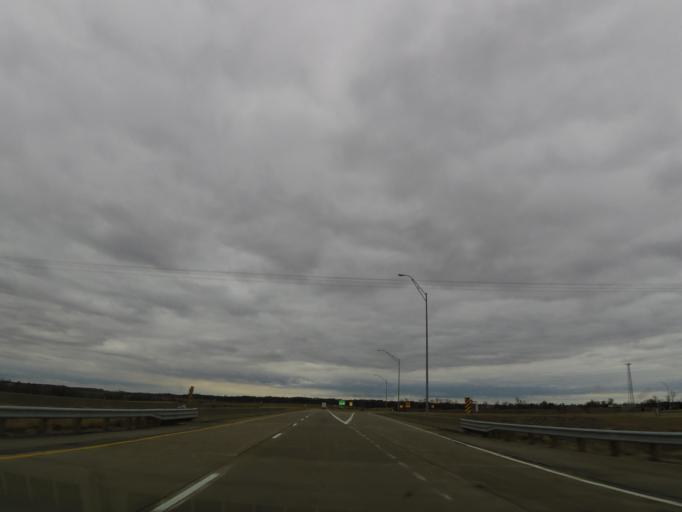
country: US
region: Iowa
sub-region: Washington County
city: Washington
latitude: 41.2919
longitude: -91.5342
